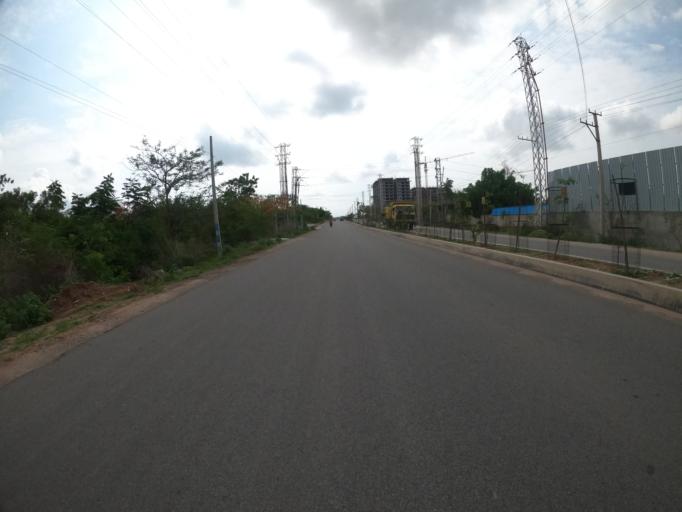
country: IN
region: Telangana
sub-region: Medak
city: Serilingampalle
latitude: 17.3906
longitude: 78.3250
